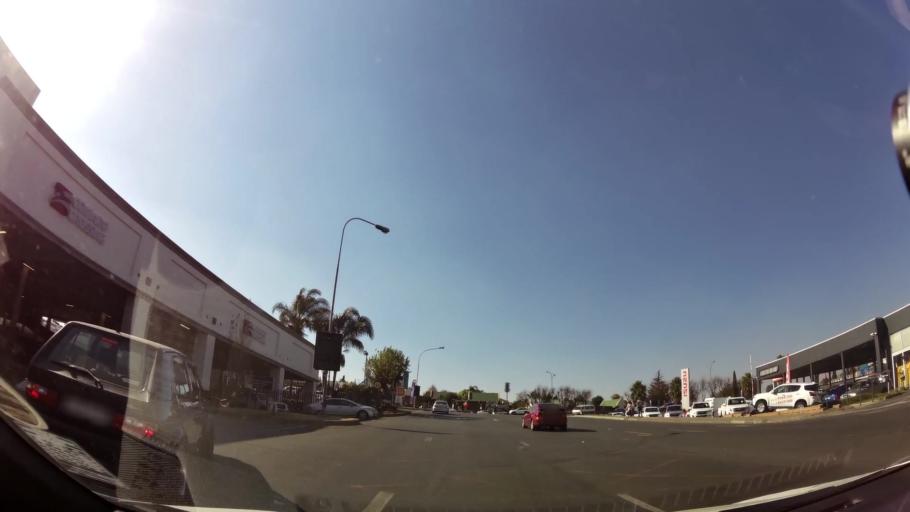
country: ZA
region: Gauteng
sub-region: City of Johannesburg Metropolitan Municipality
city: Johannesburg
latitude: -26.2668
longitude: 28.0596
